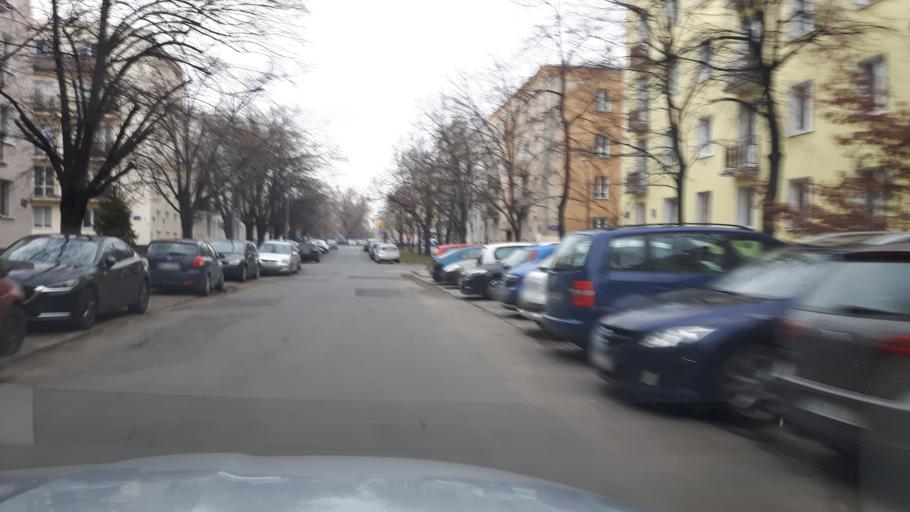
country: PL
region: Masovian Voivodeship
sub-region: Warszawa
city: Praga Poludnie
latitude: 52.2443
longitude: 21.0781
